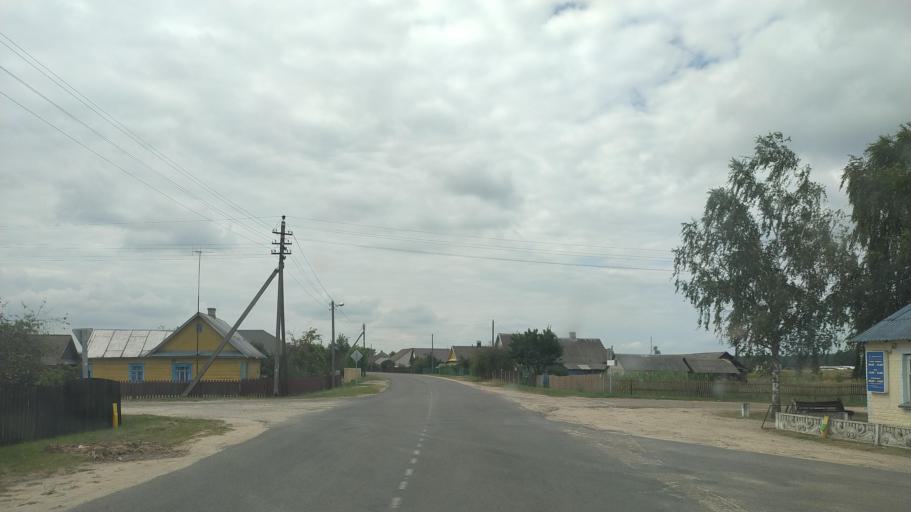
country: BY
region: Brest
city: Byaroza
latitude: 52.5421
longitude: 25.0825
